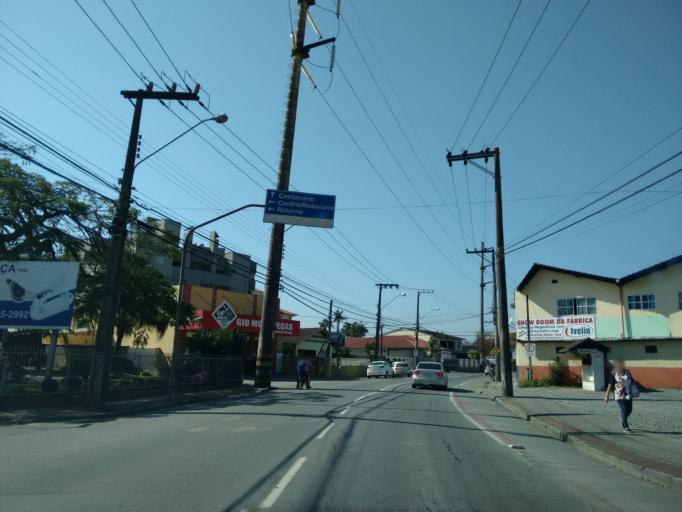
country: BR
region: Santa Catarina
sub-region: Jaragua Do Sul
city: Jaragua do Sul
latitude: -26.4927
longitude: -49.0661
